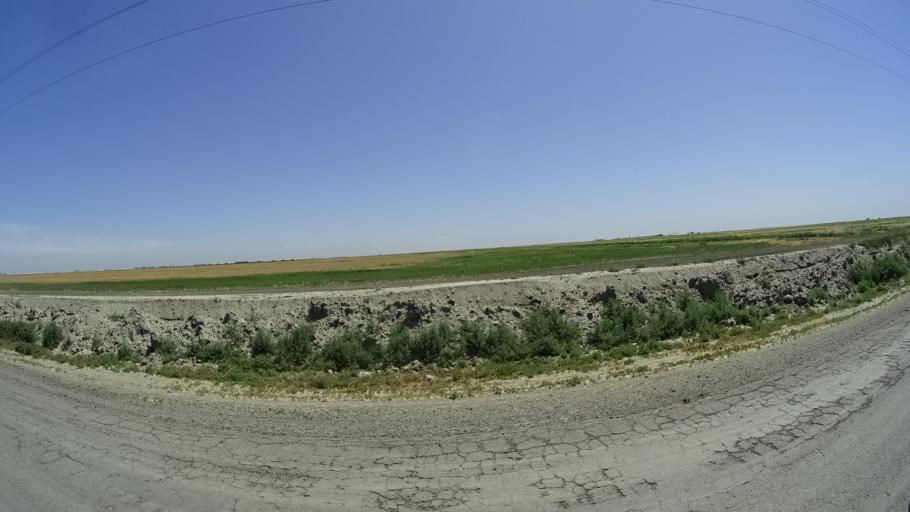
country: US
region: California
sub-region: Kings County
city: Stratford
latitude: 36.1751
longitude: -119.7175
